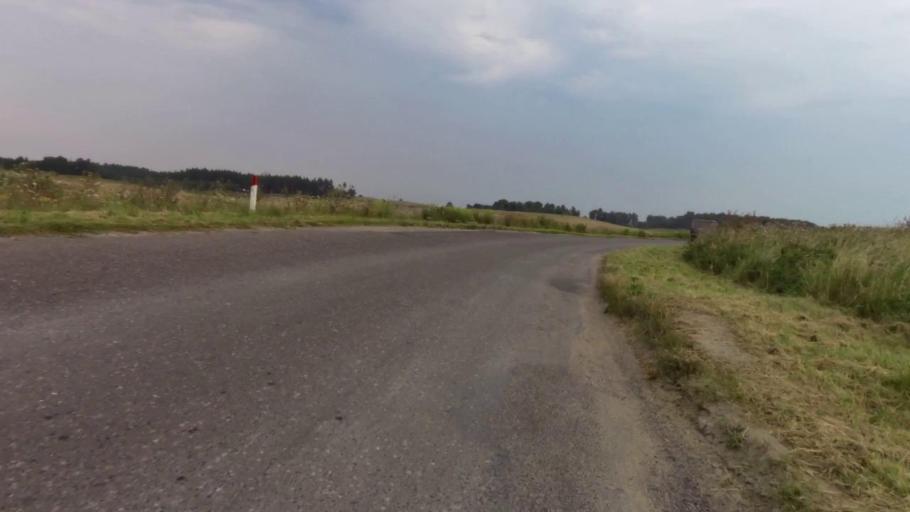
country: PL
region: West Pomeranian Voivodeship
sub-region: Powiat lobeski
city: Wegorzyno
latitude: 53.4948
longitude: 15.6277
